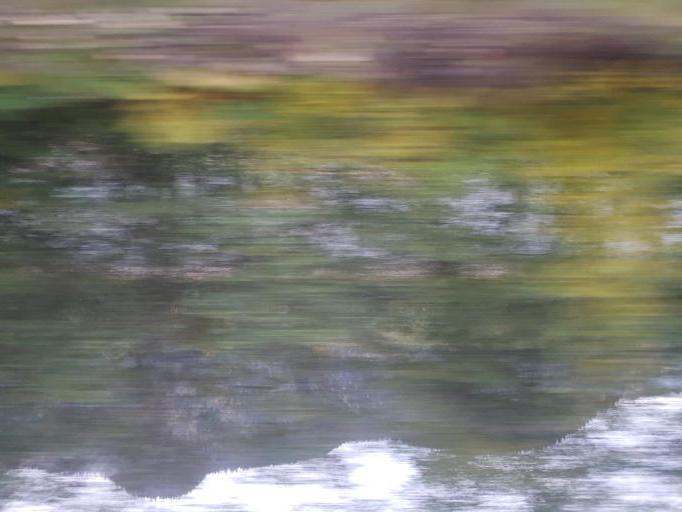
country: NO
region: Sor-Trondelag
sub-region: Midtre Gauldal
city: Storen
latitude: 63.0743
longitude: 10.2599
